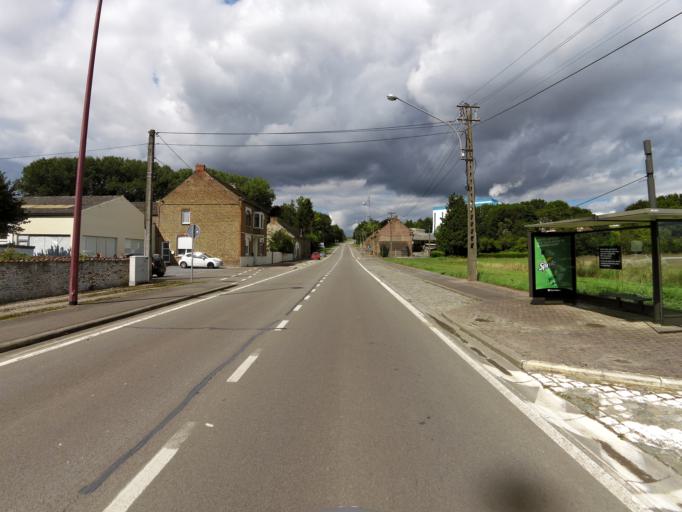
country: BE
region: Wallonia
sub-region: Province du Hainaut
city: Chasse Royale
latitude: 50.4101
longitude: 4.0099
